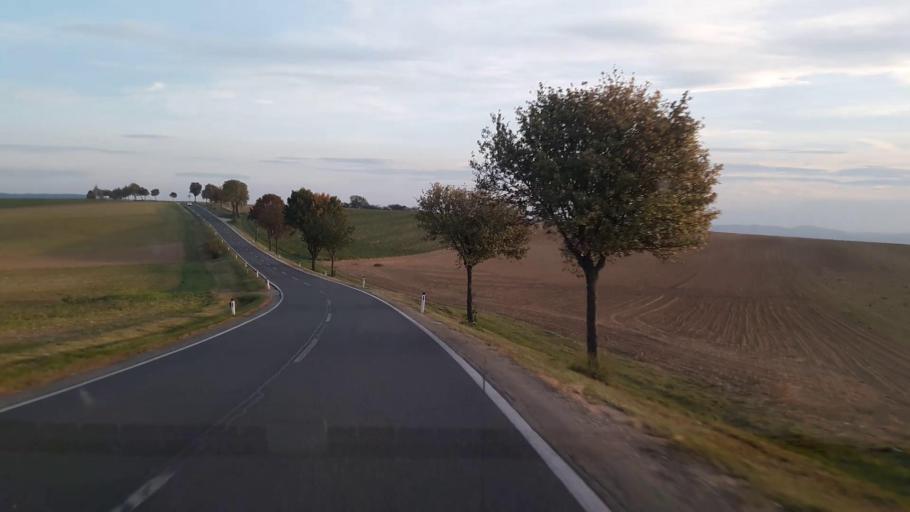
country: AT
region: Lower Austria
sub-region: Politischer Bezirk Korneuburg
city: Grossrussbach
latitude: 48.4445
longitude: 16.3876
